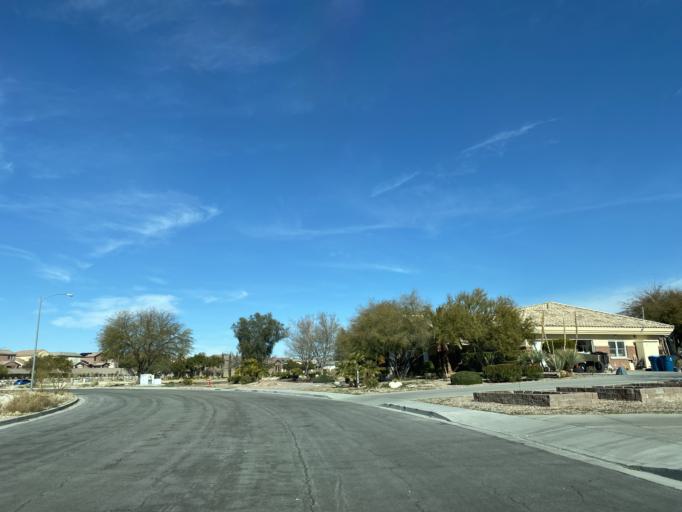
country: US
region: Nevada
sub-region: Clark County
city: North Las Vegas
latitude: 36.3080
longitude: -115.2410
